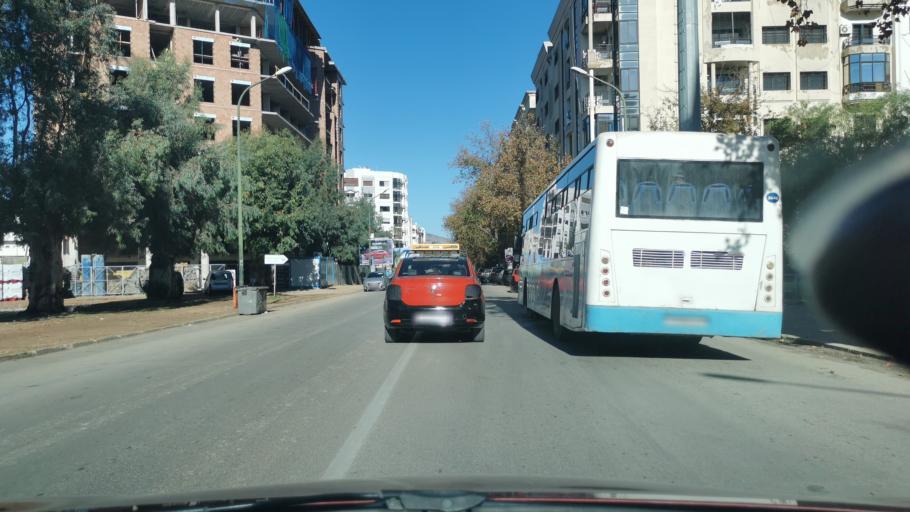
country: MA
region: Fes-Boulemane
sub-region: Fes
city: Fes
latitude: 34.0366
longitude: -5.0086
